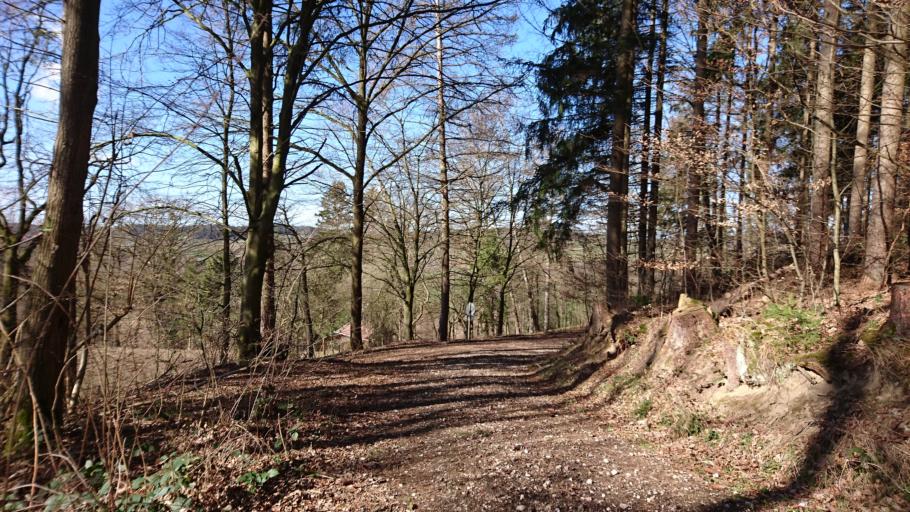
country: DE
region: Bavaria
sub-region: Swabia
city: Altenmunster
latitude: 48.4533
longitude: 10.5972
